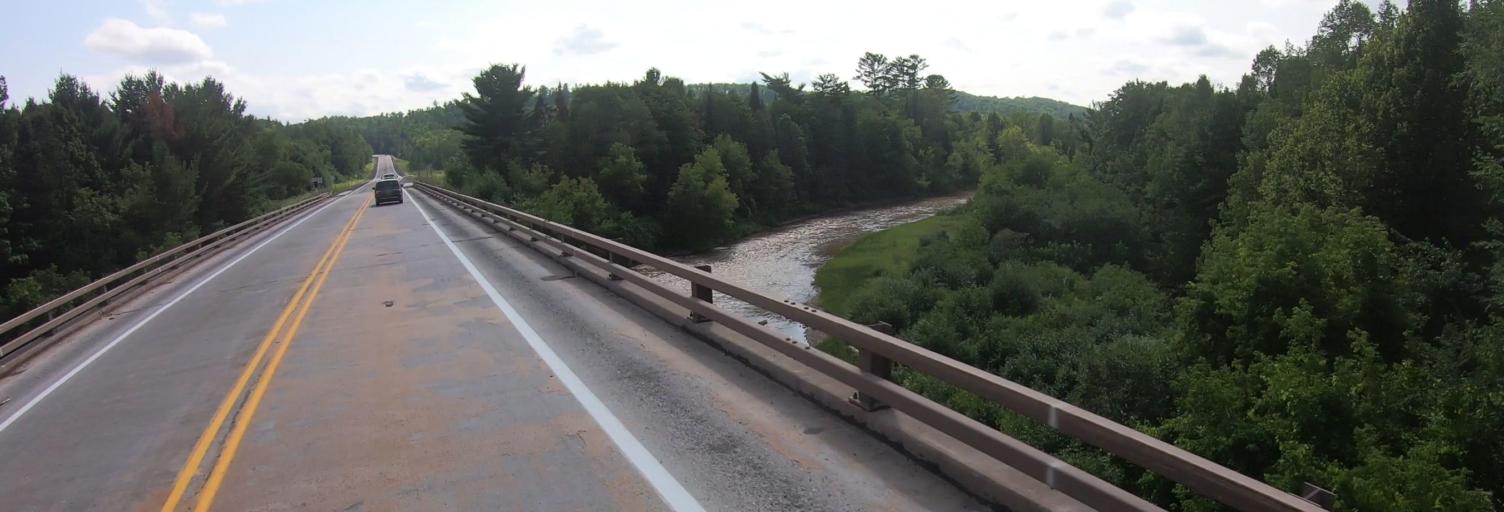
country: US
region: Michigan
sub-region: Ontonagon County
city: Ontonagon
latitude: 46.6994
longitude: -89.1600
